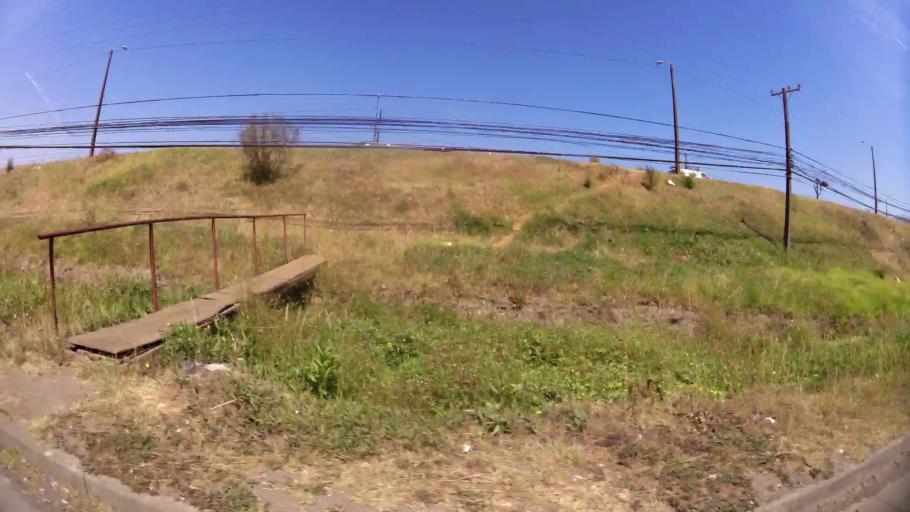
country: CL
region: Biobio
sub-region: Provincia de Concepcion
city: Concepcion
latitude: -36.8028
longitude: -73.0743
